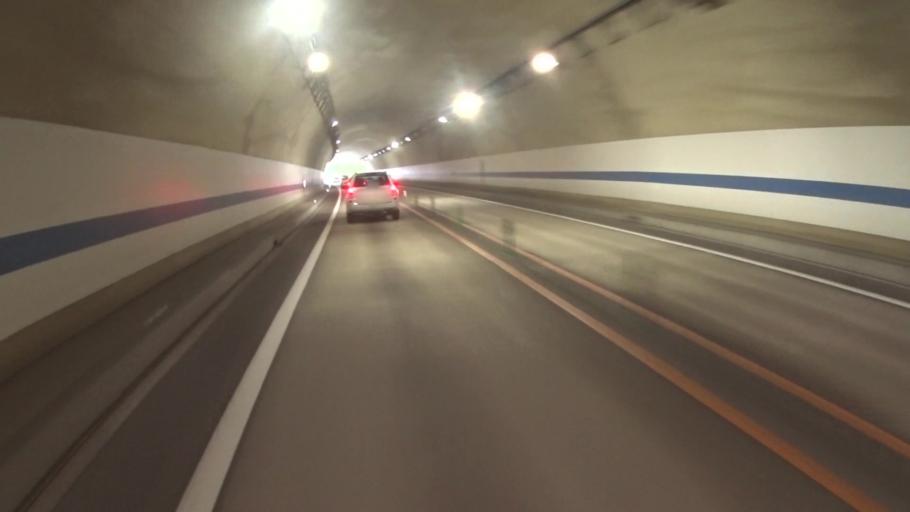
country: JP
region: Kyoto
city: Ayabe
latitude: 35.3761
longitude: 135.2646
